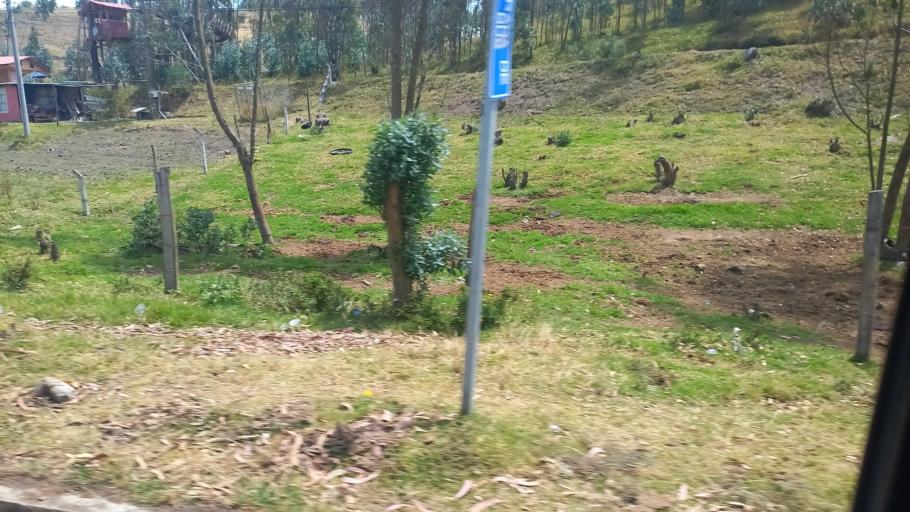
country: EC
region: Pichincha
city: Cayambe
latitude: 0.1767
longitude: -78.0910
